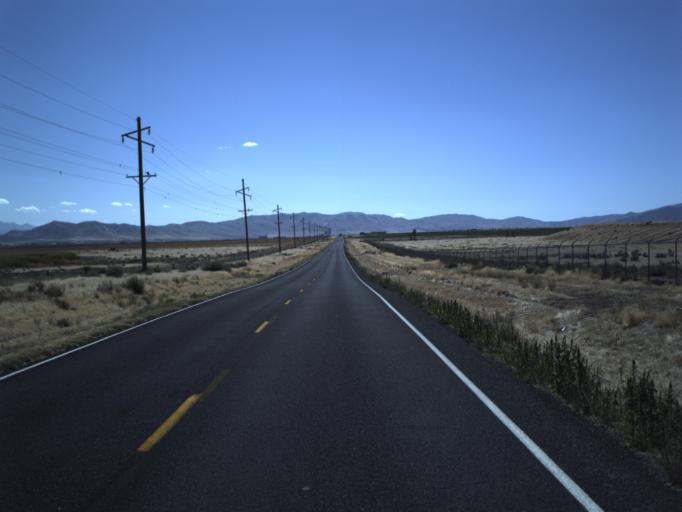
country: US
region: Utah
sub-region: Utah County
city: Genola
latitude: 40.0299
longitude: -111.9583
